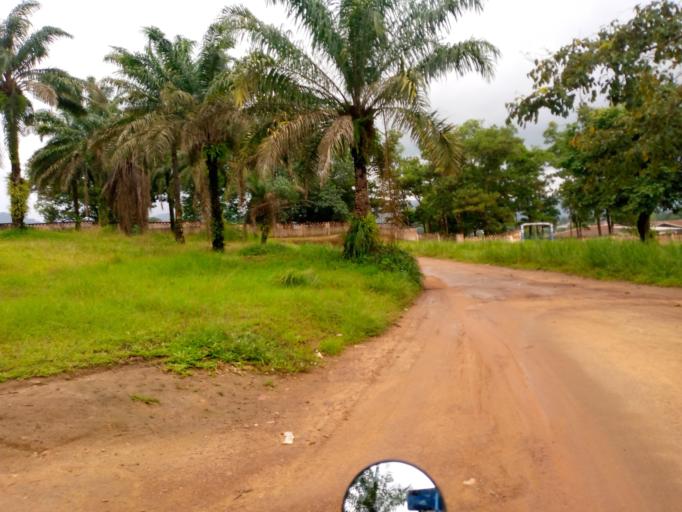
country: SL
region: Eastern Province
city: Kenema
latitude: 7.8654
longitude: -11.1849
